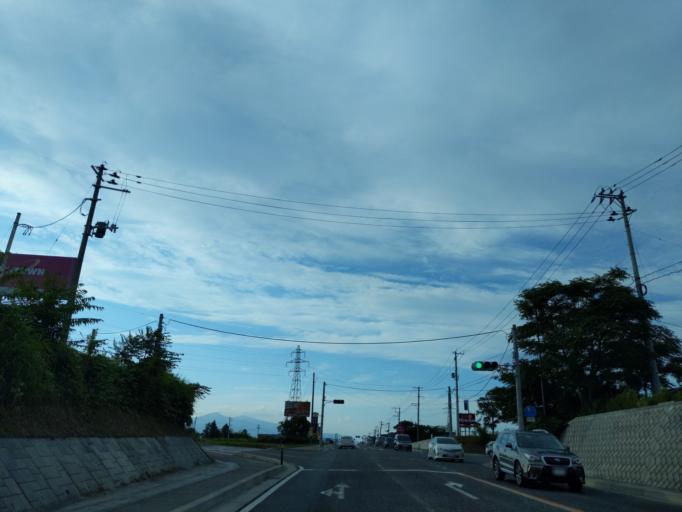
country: JP
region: Fukushima
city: Koriyama
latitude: 37.4350
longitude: 140.3809
